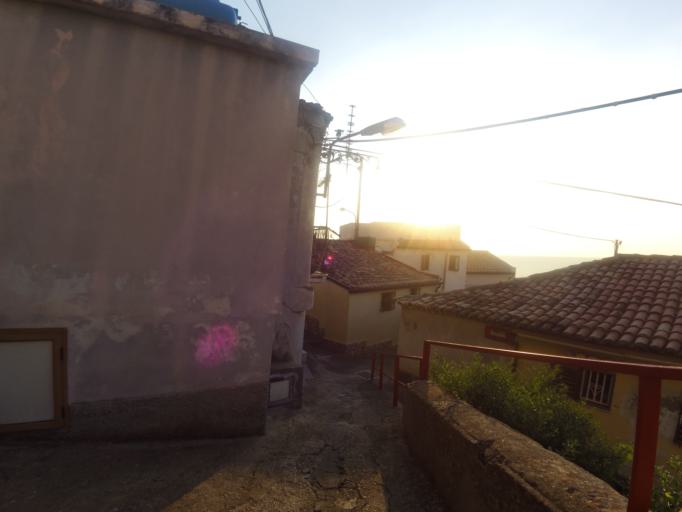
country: IT
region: Calabria
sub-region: Provincia di Vibo-Valentia
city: Maierato
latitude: 38.7343
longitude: 16.1617
